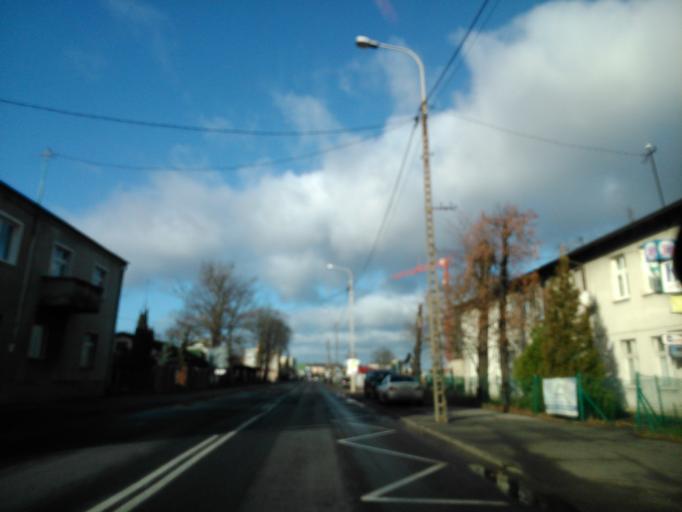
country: PL
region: Kujawsko-Pomorskie
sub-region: Torun
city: Torun
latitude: 52.9944
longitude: 18.6283
